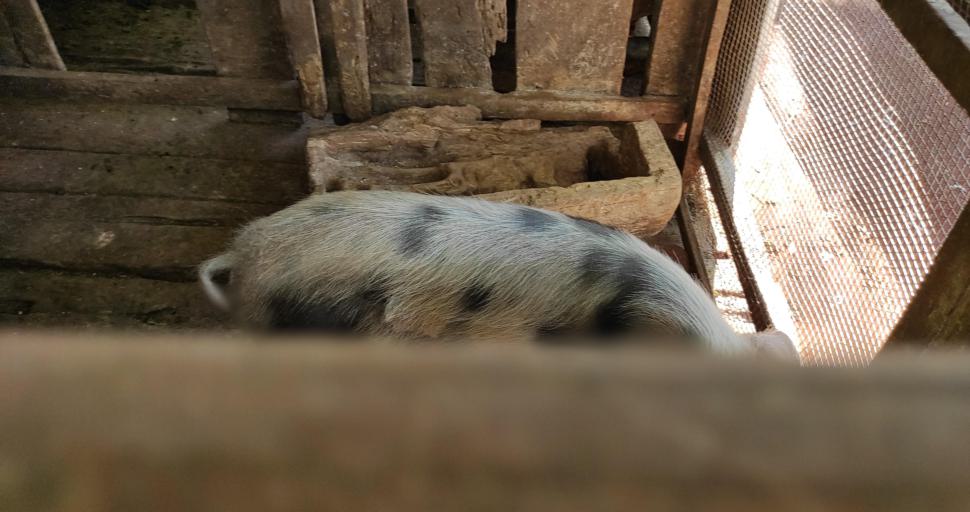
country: AR
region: Misiones
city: Capiovi
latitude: -26.9145
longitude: -55.0946
